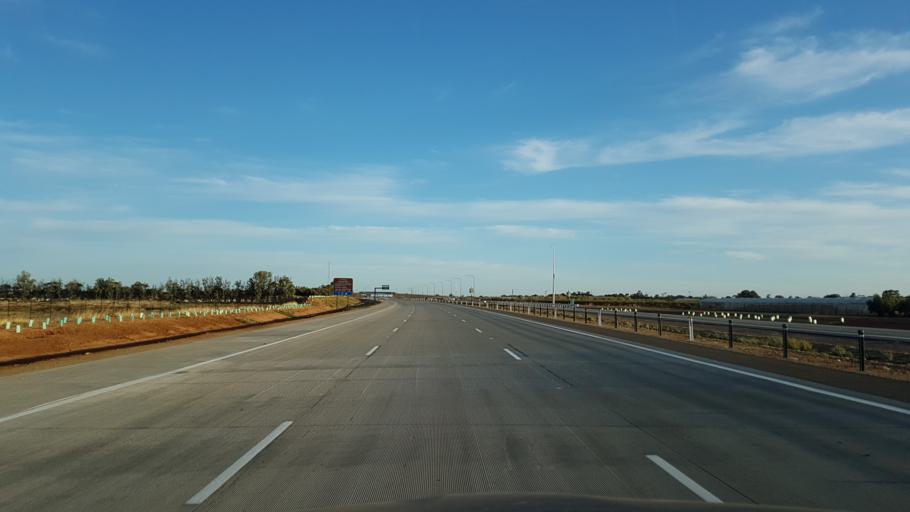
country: AU
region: South Australia
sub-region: Salisbury
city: Salisbury
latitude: -34.7440
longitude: 138.5801
